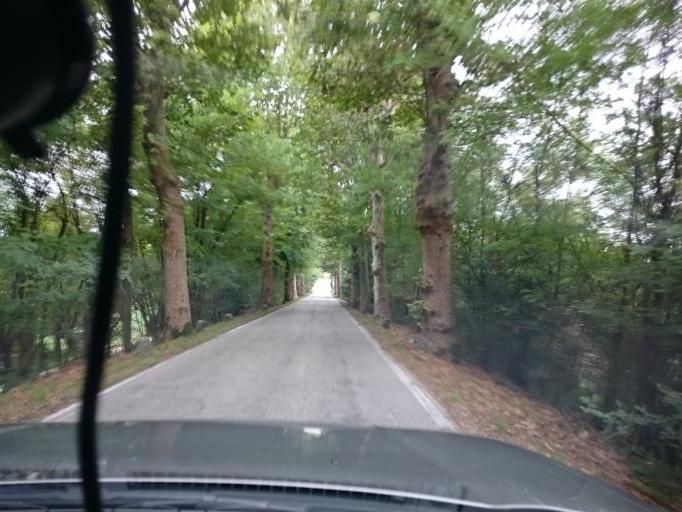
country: IT
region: Veneto
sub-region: Provincia di Vicenza
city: Grisignano di Zocco
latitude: 45.4846
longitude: 11.7162
